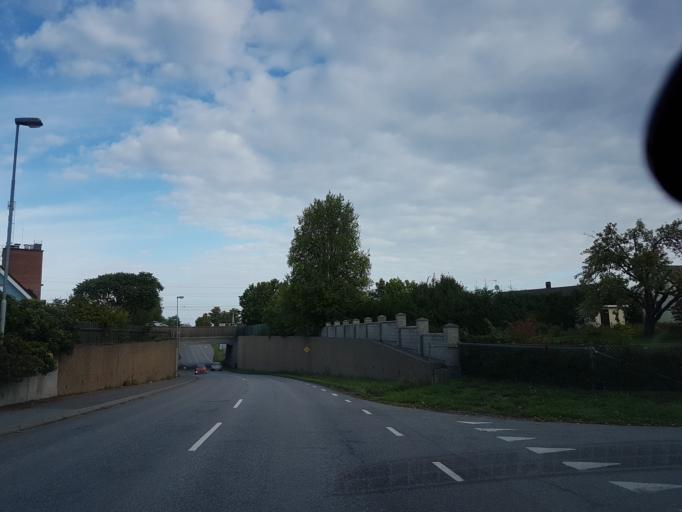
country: SE
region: OEstergoetland
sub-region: Linkopings Kommun
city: Vikingstad
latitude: 58.3835
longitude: 15.4364
